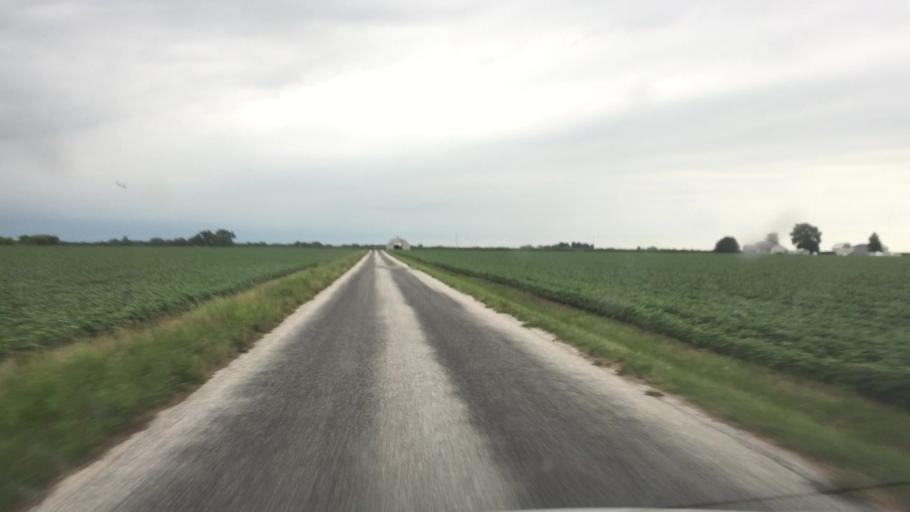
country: US
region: Illinois
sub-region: Adams County
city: Camp Point
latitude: 40.2253
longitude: -90.9690
